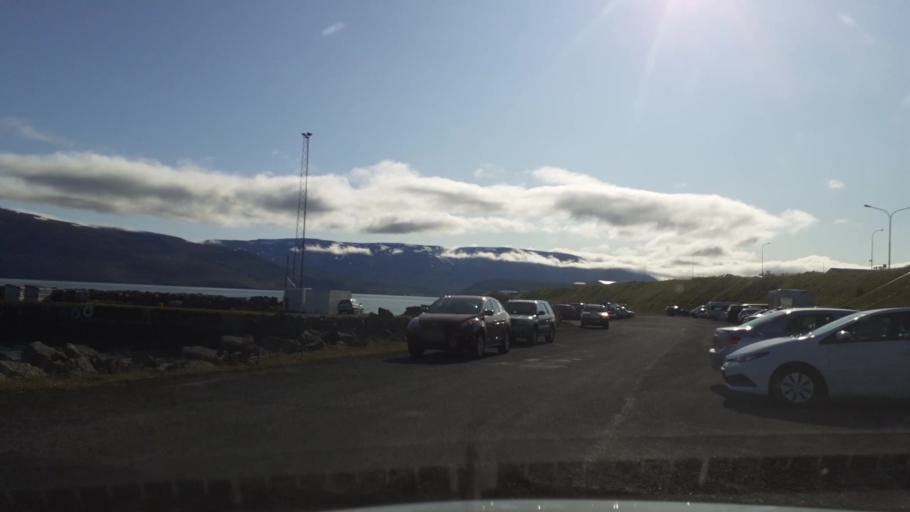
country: IS
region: Northeast
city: Dalvik
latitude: 65.9456
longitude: -18.3571
